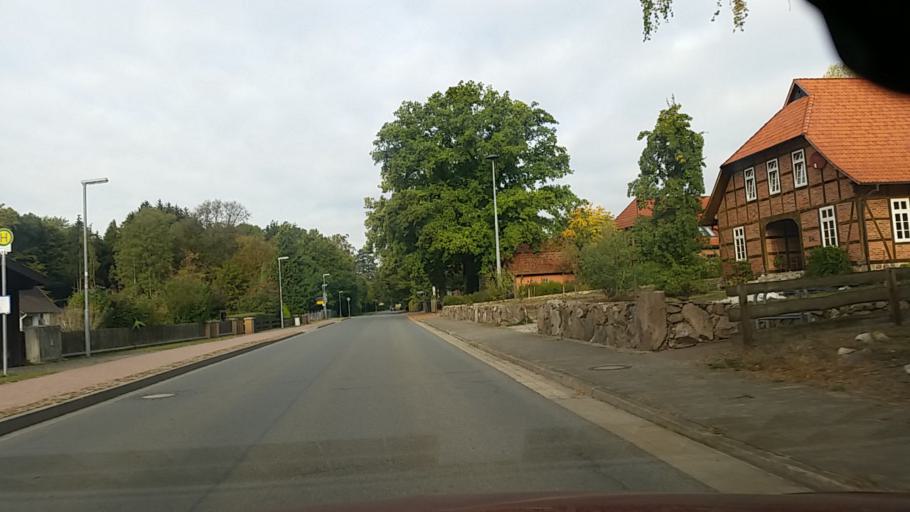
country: DE
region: Lower Saxony
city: Ahnsbeck
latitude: 52.5918
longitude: 10.3258
